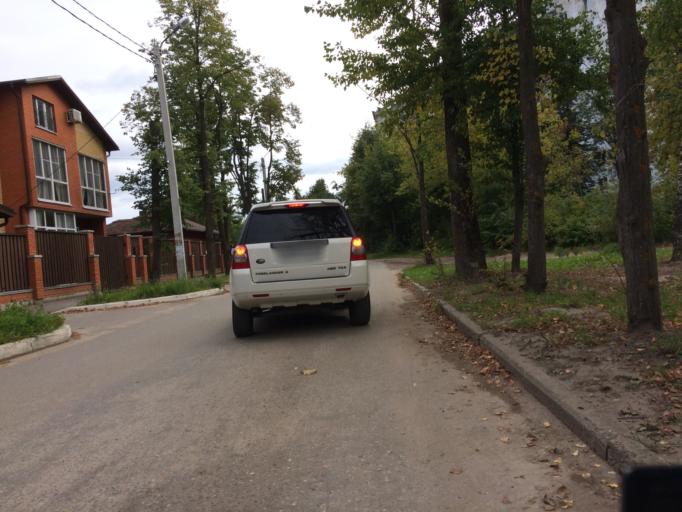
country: RU
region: Mariy-El
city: Yoshkar-Ola
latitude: 56.6511
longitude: 47.9727
